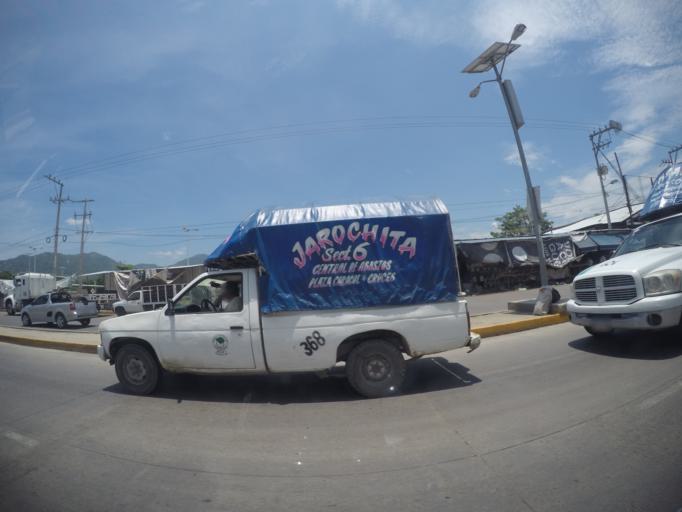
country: MX
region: Guerrero
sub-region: Acapulco de Juarez
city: Nueva Frontera
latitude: 16.8994
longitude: -99.8301
